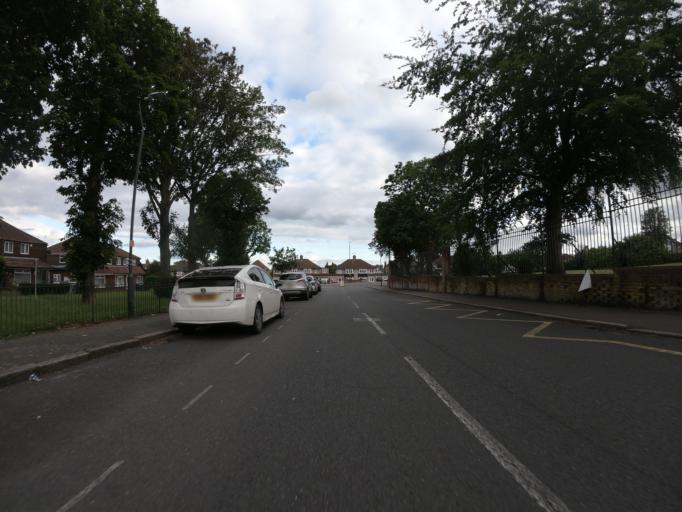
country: GB
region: England
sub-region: Greater London
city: Bexleyheath
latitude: 51.4785
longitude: 0.1357
